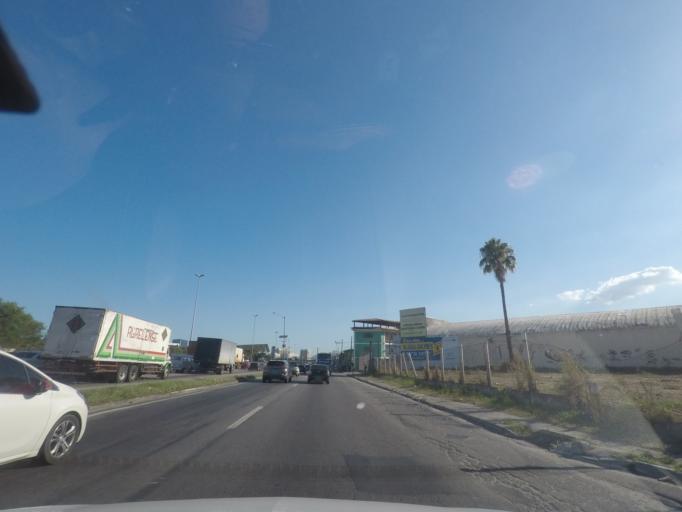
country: BR
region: Rio de Janeiro
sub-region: Duque De Caxias
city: Duque de Caxias
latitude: -22.7807
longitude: -43.2859
